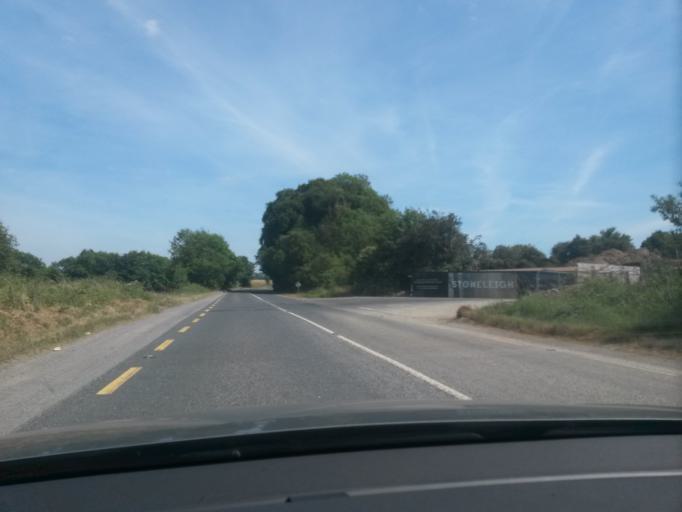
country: IE
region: Leinster
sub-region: Kildare
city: Naas
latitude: 53.2096
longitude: -6.6422
